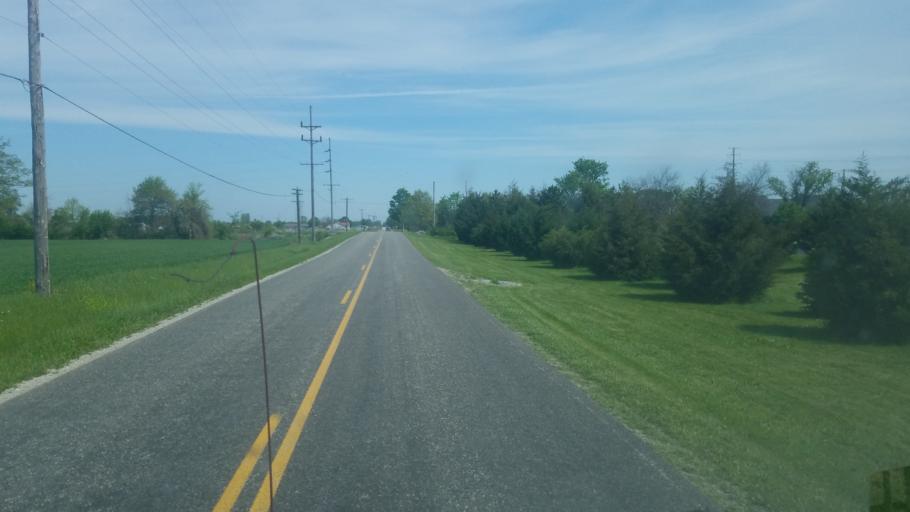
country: US
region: Ohio
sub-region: Seneca County
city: Tiffin
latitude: 41.1046
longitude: -83.1313
